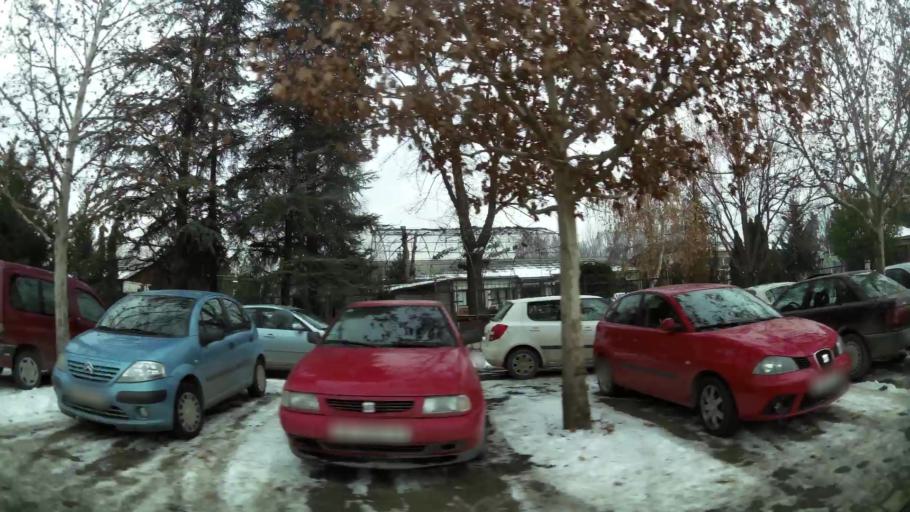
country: MK
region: Butel
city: Butel
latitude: 42.0309
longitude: 21.4358
